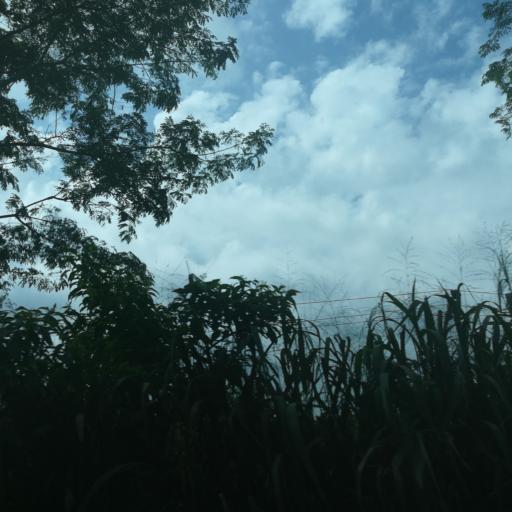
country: NG
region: Lagos
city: Ikorodu
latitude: 6.6636
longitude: 3.6346
